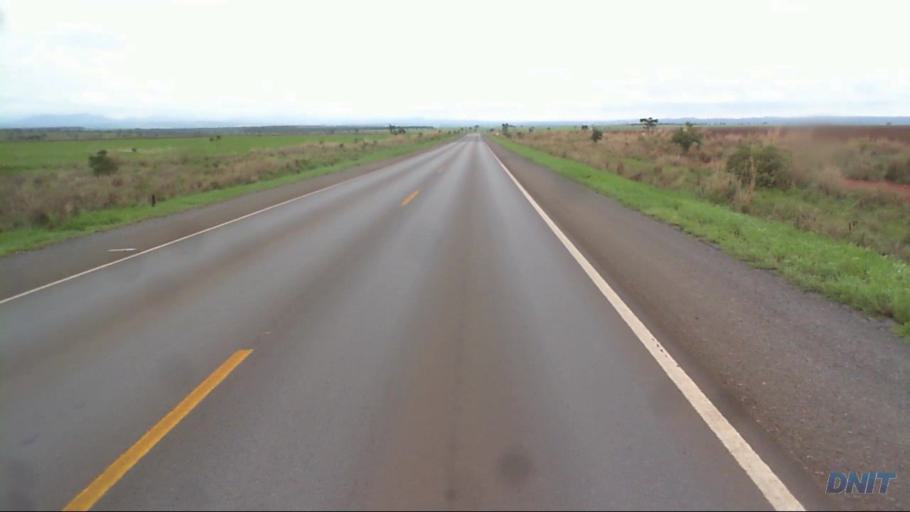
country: BR
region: Goias
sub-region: Padre Bernardo
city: Padre Bernardo
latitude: -15.1741
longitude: -48.3967
